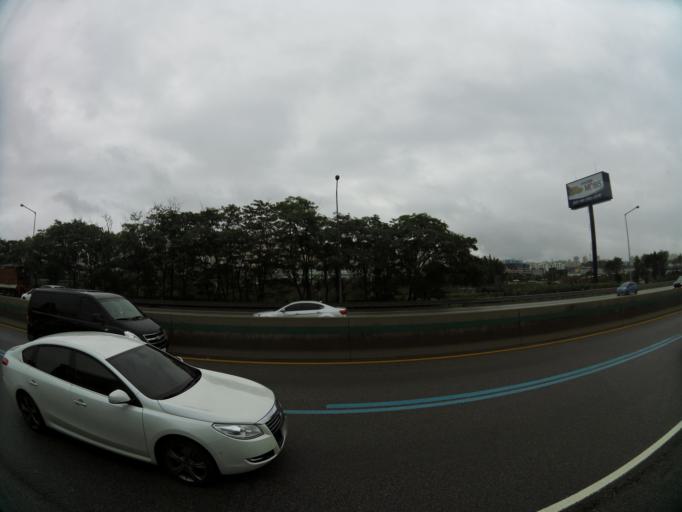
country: KR
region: Gyeonggi-do
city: Suwon-si
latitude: 37.3002
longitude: 127.1036
